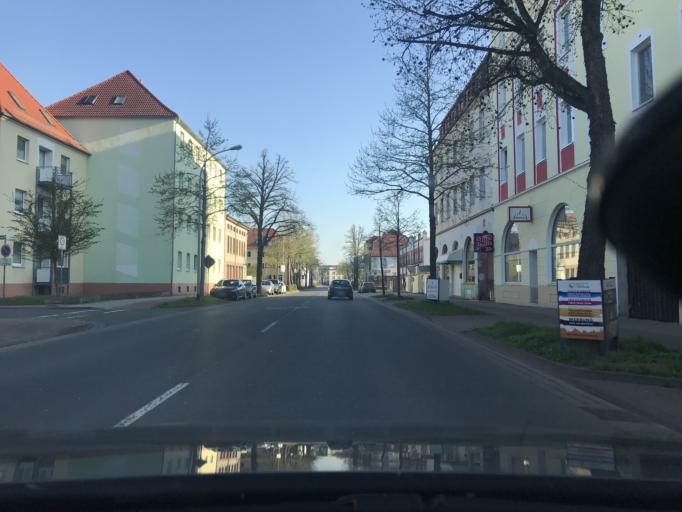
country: DE
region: Thuringia
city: Nordhausen
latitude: 51.4998
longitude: 10.7820
